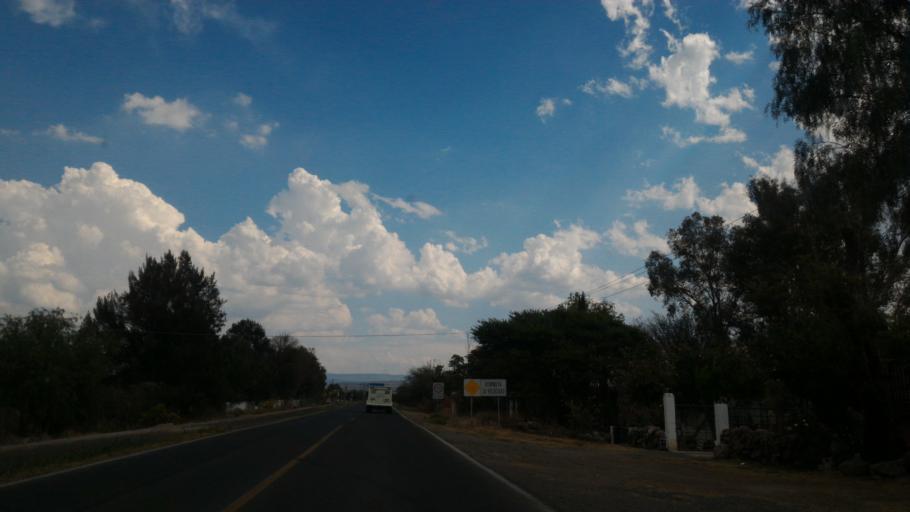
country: MX
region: Guanajuato
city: Ciudad Manuel Doblado
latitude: 20.7465
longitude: -101.9597
